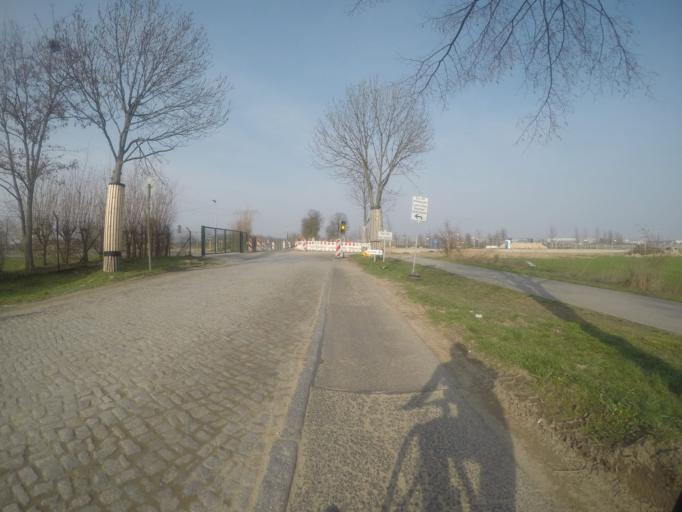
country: DE
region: Berlin
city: Rudow
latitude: 52.3869
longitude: 13.4786
